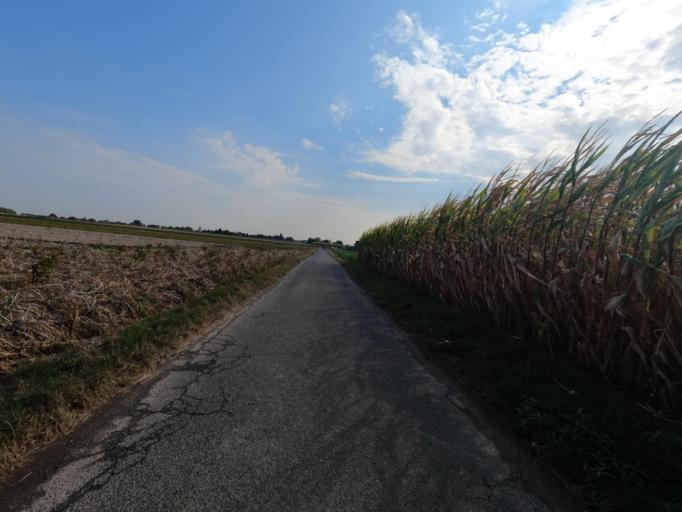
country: DE
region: North Rhine-Westphalia
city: Huckelhoven
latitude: 51.0965
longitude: 6.2291
